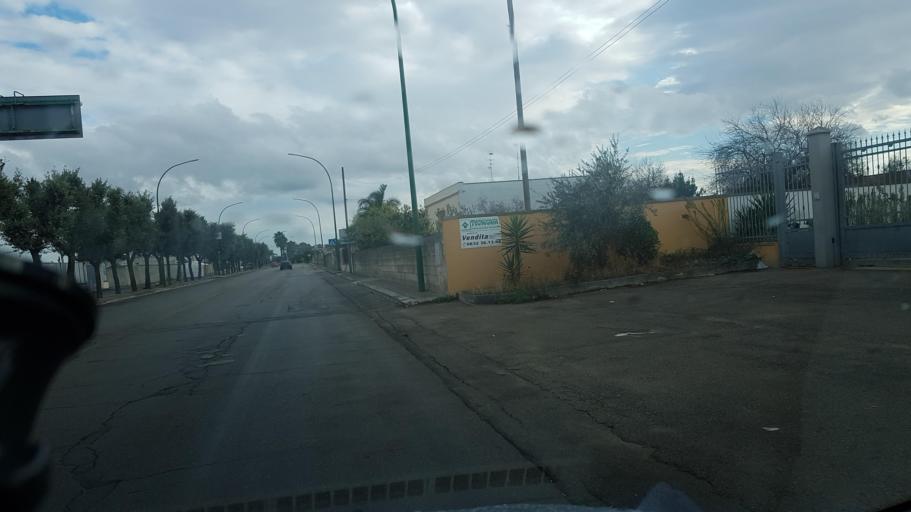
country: IT
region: Apulia
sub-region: Provincia di Lecce
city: Surbo
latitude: 40.3844
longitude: 18.1351
